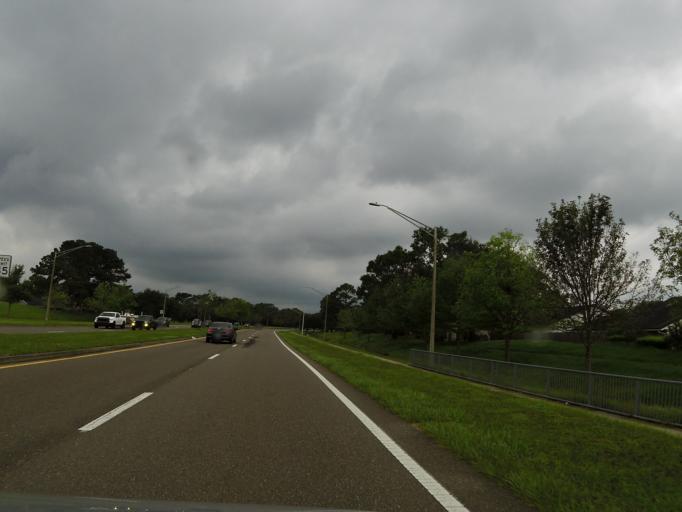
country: US
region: Florida
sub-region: Clay County
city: Bellair-Meadowbrook Terrace
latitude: 30.1929
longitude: -81.7875
